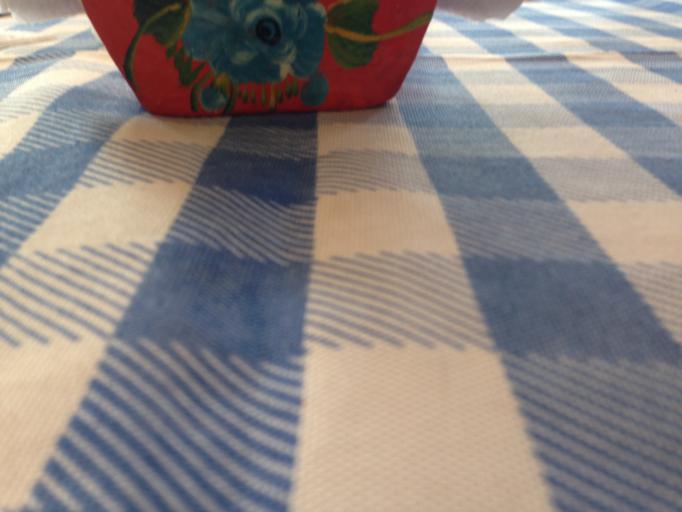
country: MX
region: Morelos
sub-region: Cuernavaca
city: Lomas de Ahuatepec
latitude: 18.9697
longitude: -99.2156
